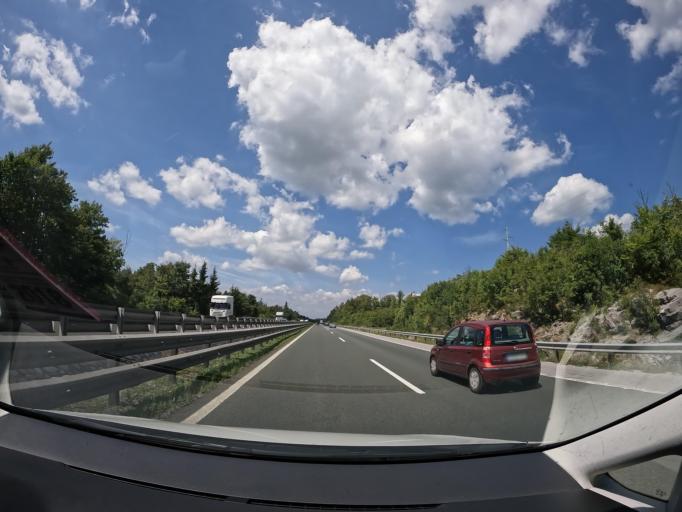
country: SI
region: Cerknica
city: Rakek
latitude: 45.8567
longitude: 14.2782
